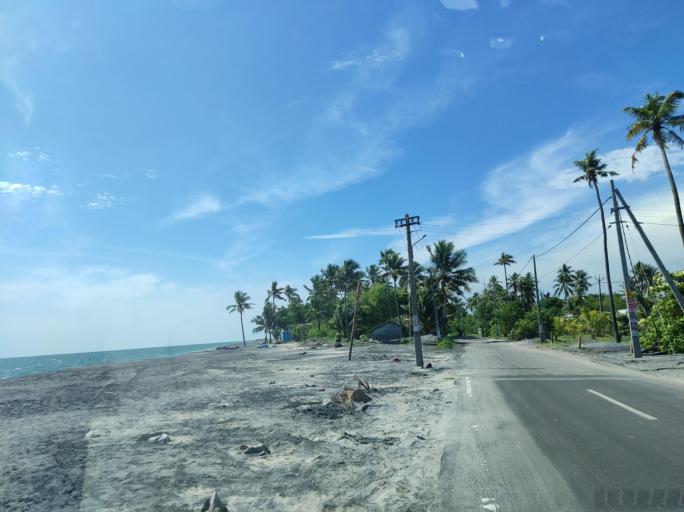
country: IN
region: Kerala
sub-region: Alappuzha
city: Kayankulam
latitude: 9.1674
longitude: 76.4492
